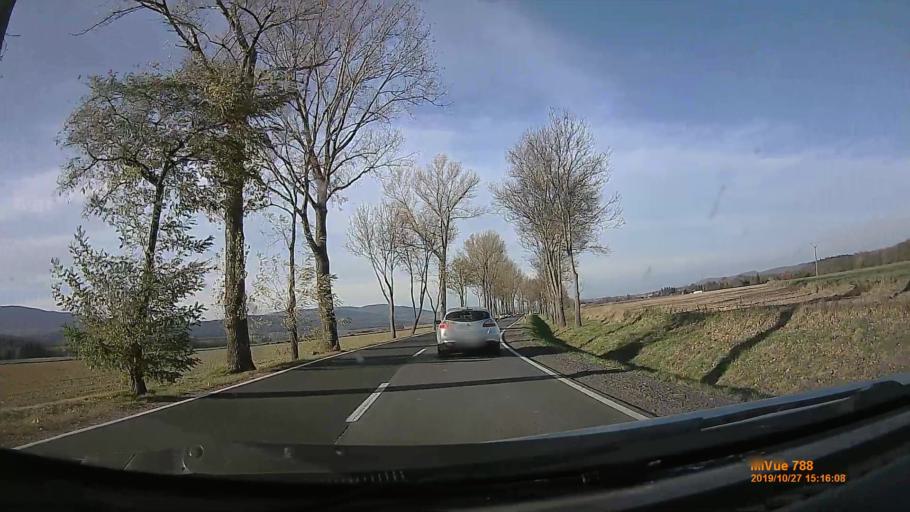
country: PL
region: Lower Silesian Voivodeship
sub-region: Powiat klodzki
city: Bystrzyca Klodzka
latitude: 50.2449
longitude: 16.6702
